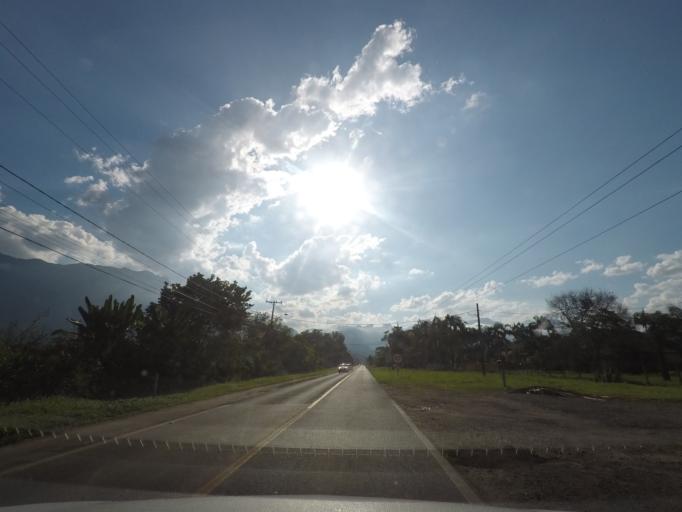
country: BR
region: Parana
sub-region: Antonina
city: Antonina
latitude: -25.4590
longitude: -48.8565
